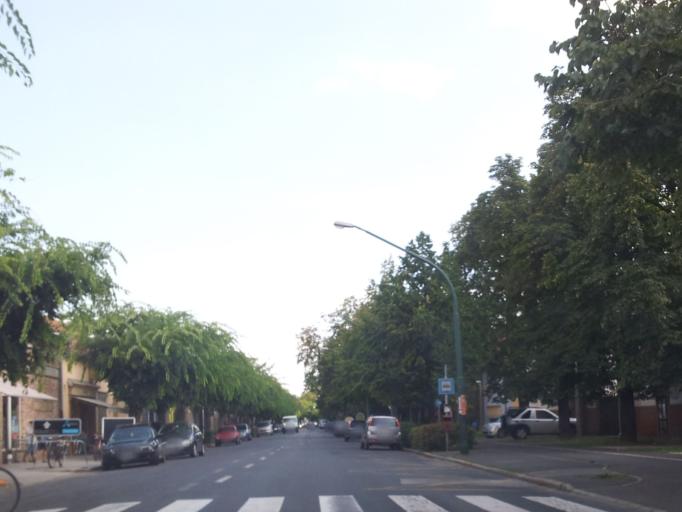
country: HU
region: Baranya
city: Mohacs
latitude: 45.9912
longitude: 18.6818
